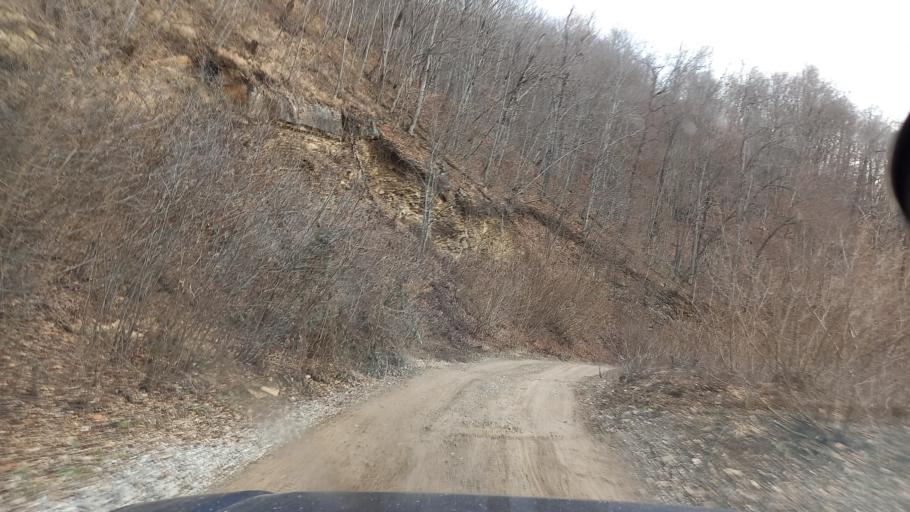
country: RU
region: Adygeya
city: Kamennomostskiy
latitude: 44.1650
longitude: 40.3007
